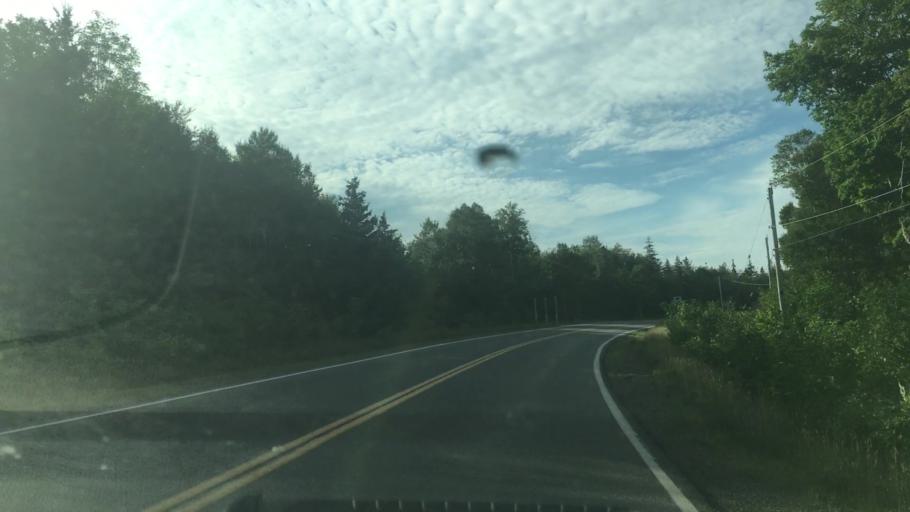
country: CA
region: Nova Scotia
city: Sydney Mines
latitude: 46.8178
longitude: -60.7943
